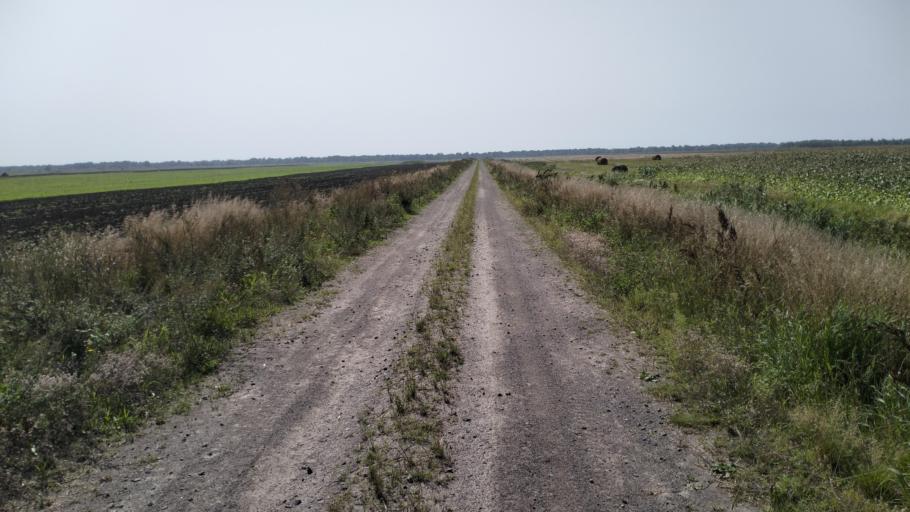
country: BY
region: Brest
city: Davyd-Haradok
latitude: 51.9850
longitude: 27.1637
